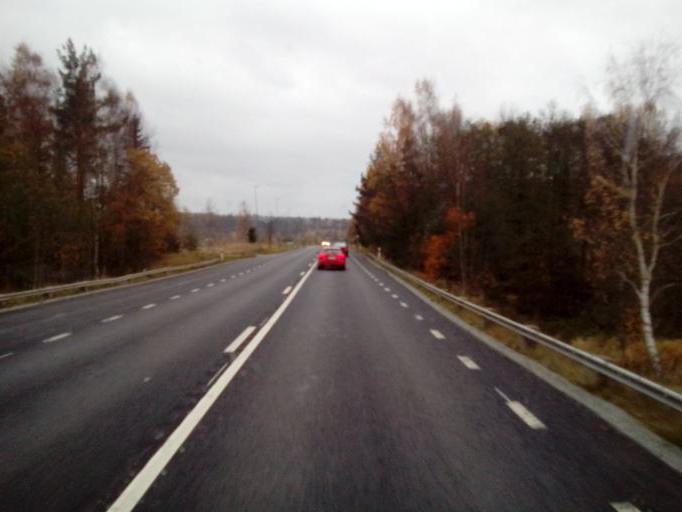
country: SE
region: OErebro
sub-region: Degerfors Kommun
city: Degerfors
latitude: 59.2619
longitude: 14.4406
